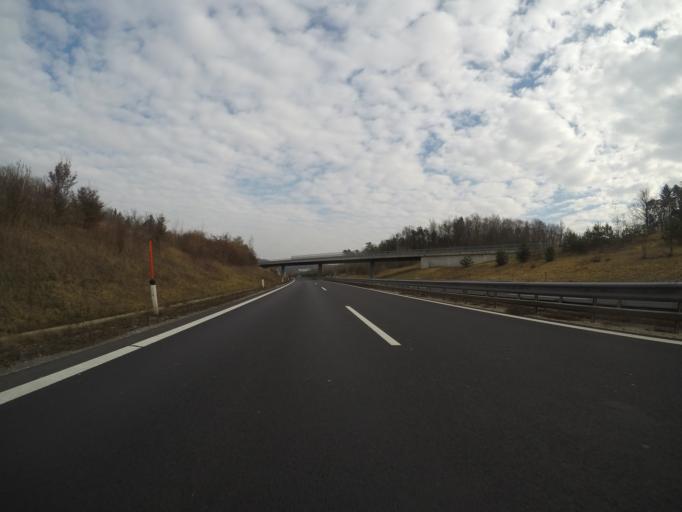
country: SI
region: Sveta Trojica v Slovenskih Goricah
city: Sv. Trojica v Slov. Goricah
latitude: 46.5558
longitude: 15.8969
